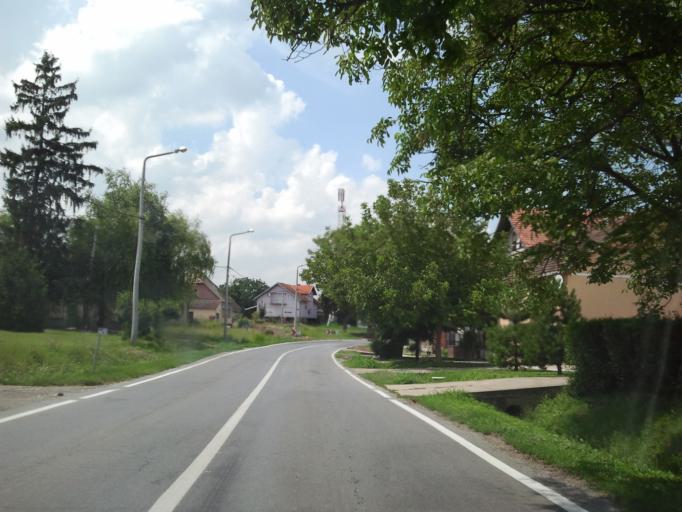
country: HR
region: Vukovarsko-Srijemska
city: Lovas
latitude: 45.2953
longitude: 19.0979
